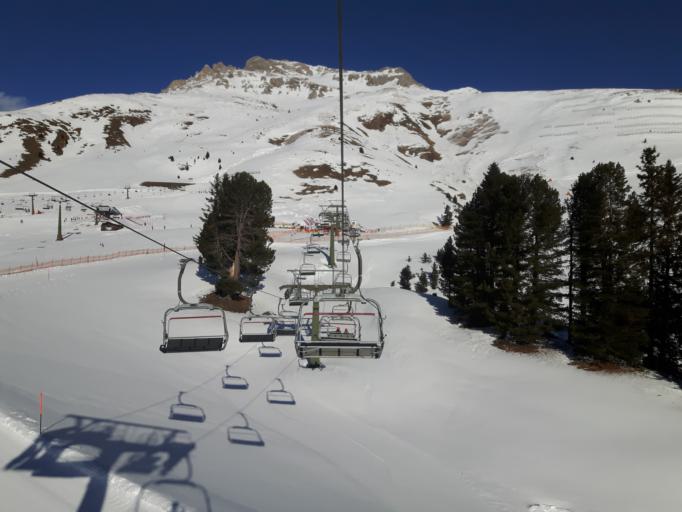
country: IT
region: Trentino-Alto Adige
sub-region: Provincia di Trento
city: Panchia
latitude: 46.3477
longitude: 11.5461
